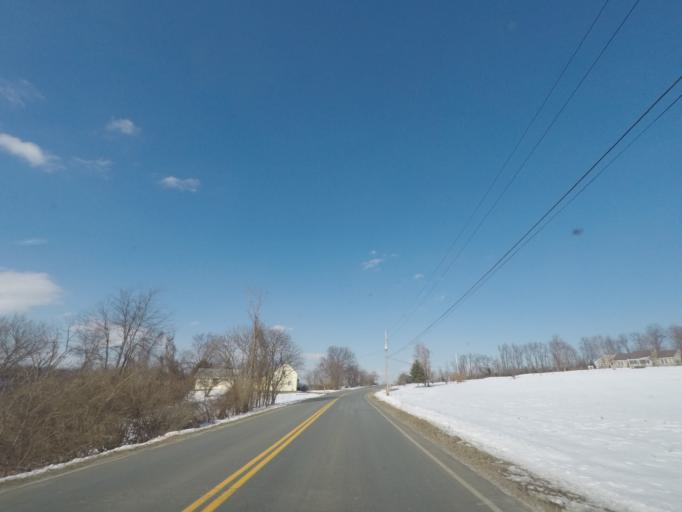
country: US
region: New York
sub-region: Saratoga County
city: Stillwater
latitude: 42.8586
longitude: -73.5983
